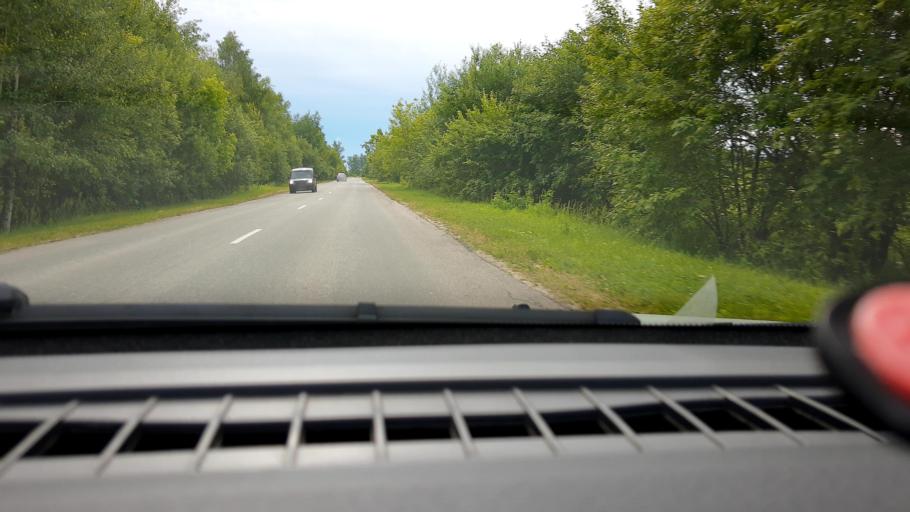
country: RU
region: Nizjnij Novgorod
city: Kstovo
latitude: 56.1496
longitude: 44.3009
